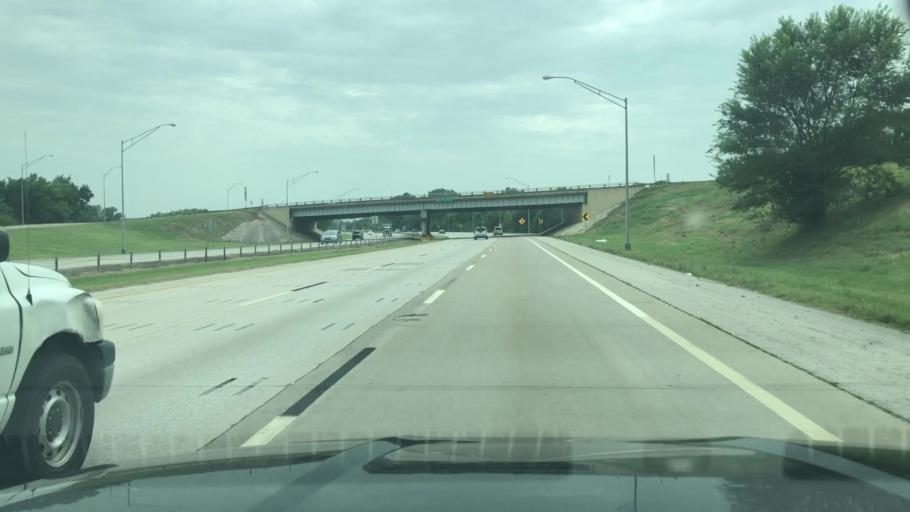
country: US
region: Oklahoma
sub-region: Tulsa County
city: Sand Springs
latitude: 36.1530
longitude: -96.0637
